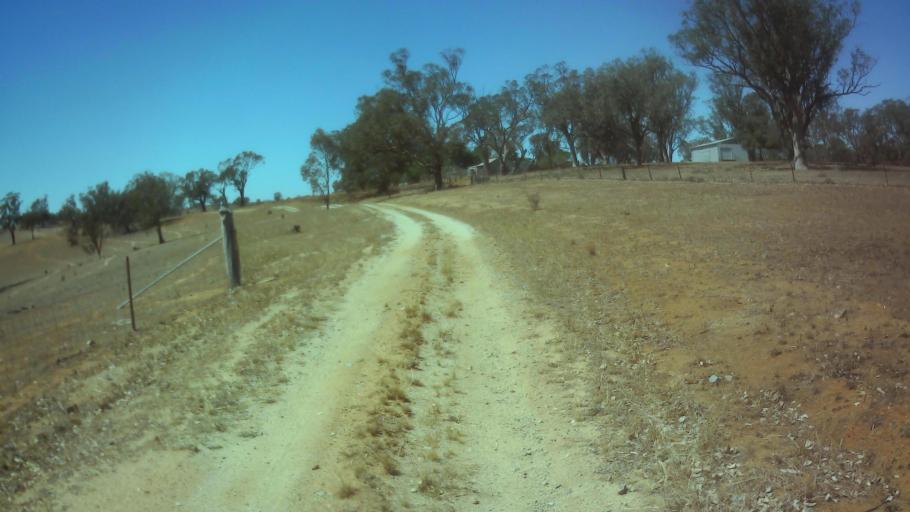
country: AU
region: New South Wales
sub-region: Cowra
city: Cowra
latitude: -33.8877
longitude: 148.4981
